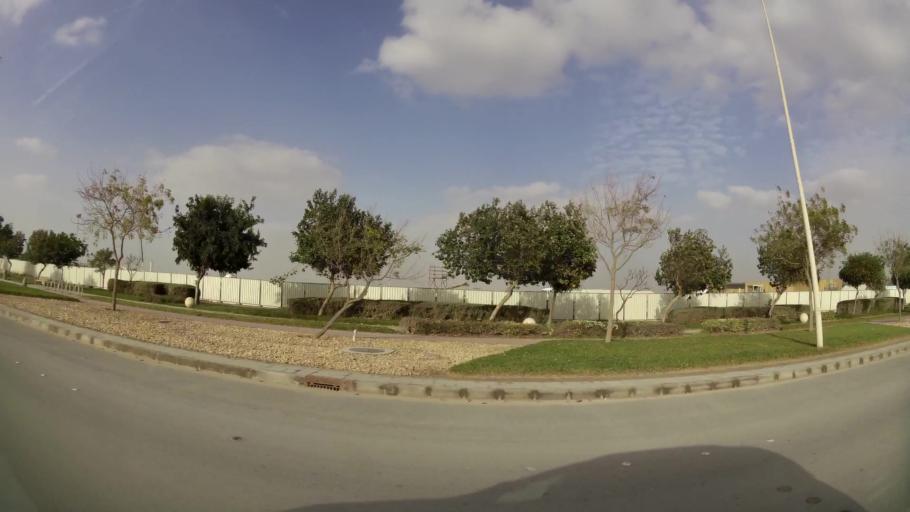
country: AE
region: Abu Dhabi
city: Abu Dhabi
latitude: 24.4913
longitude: 54.5922
